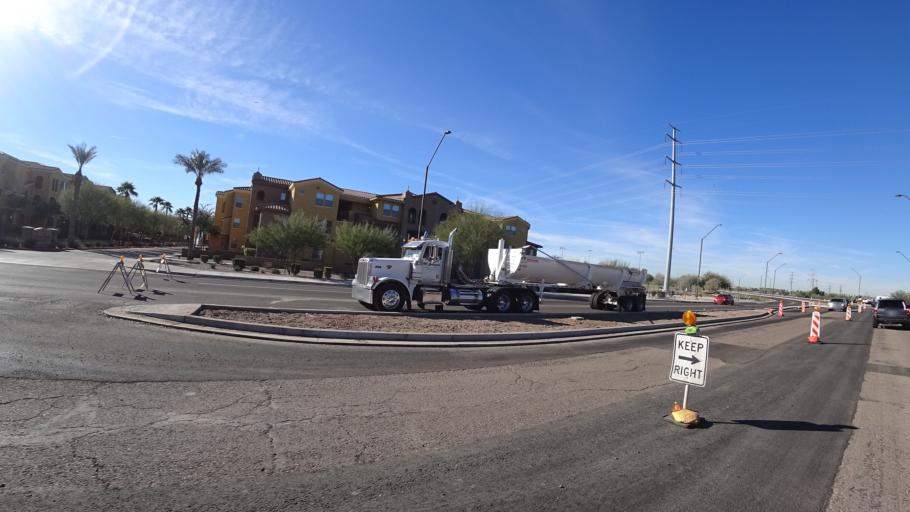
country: US
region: Arizona
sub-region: Maricopa County
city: Avondale
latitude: 33.4641
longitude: -112.3179
